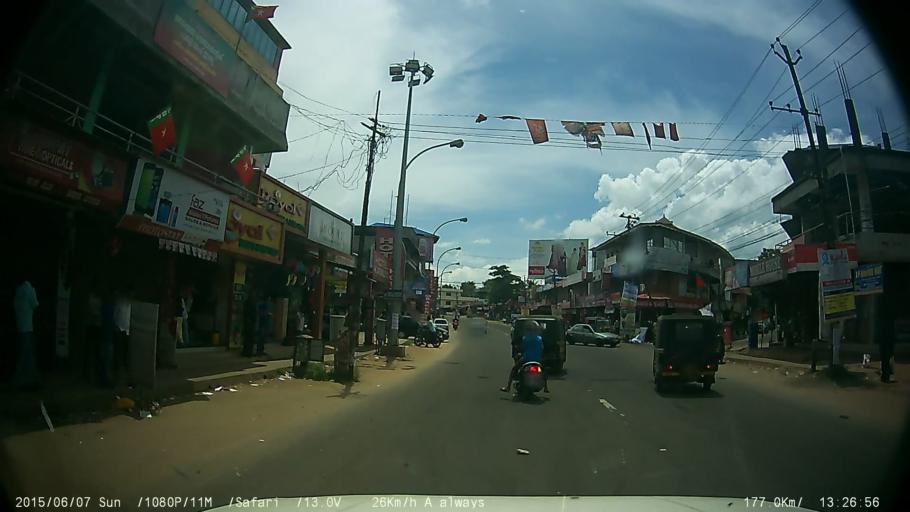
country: IN
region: Kerala
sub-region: Ernakulam
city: Muvattupula
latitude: 10.0178
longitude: 76.5641
